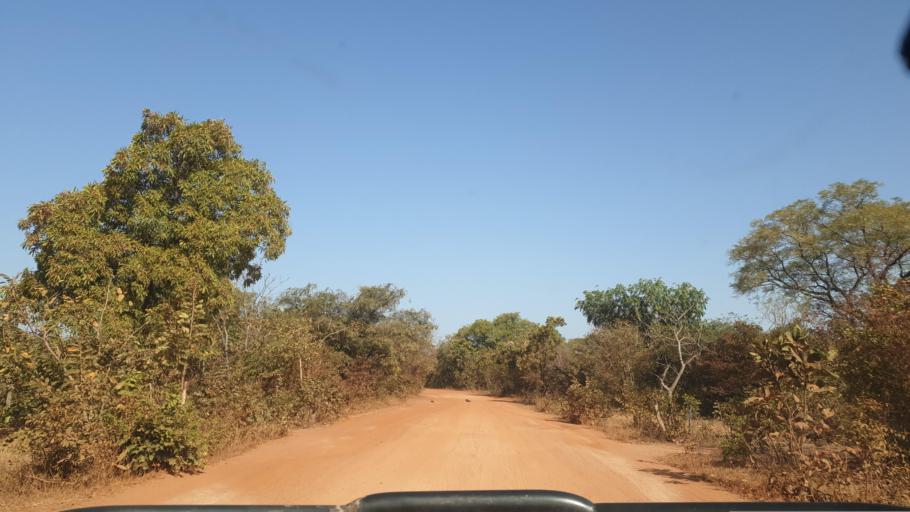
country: ML
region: Sikasso
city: Bougouni
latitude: 11.7829
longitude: -6.9085
